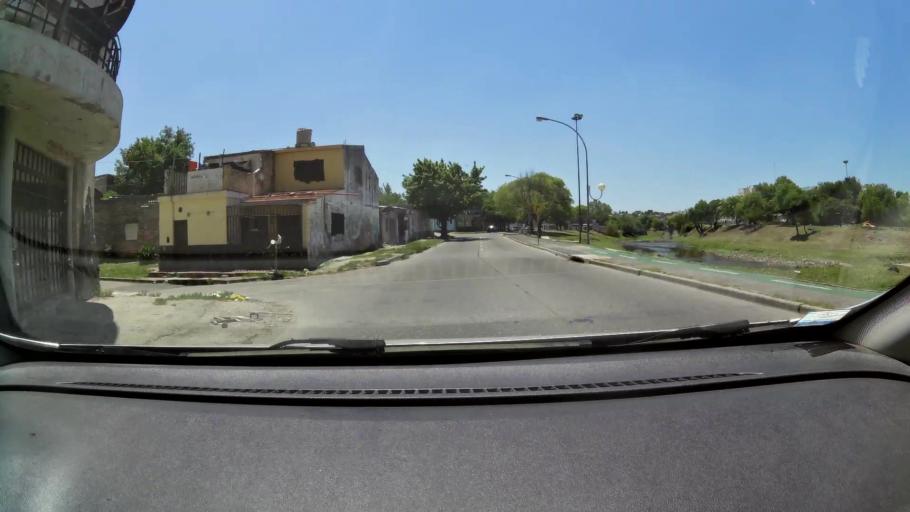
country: AR
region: Cordoba
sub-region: Departamento de Capital
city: Cordoba
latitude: -31.4001
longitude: -64.2048
